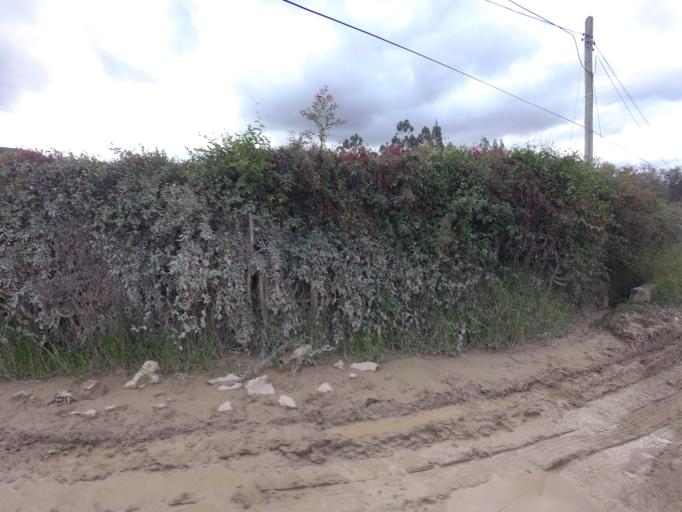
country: CO
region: Cundinamarca
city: Tabio
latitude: 4.9300
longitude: -74.0922
